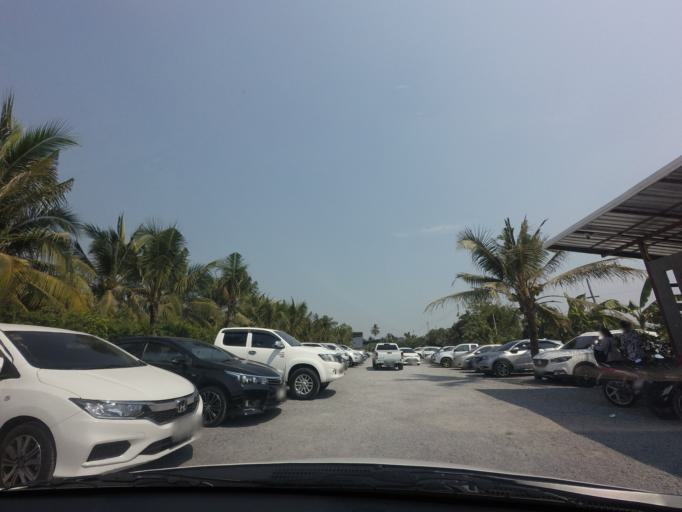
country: TH
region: Nakhon Pathom
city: Sam Phran
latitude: 13.7279
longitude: 100.2660
